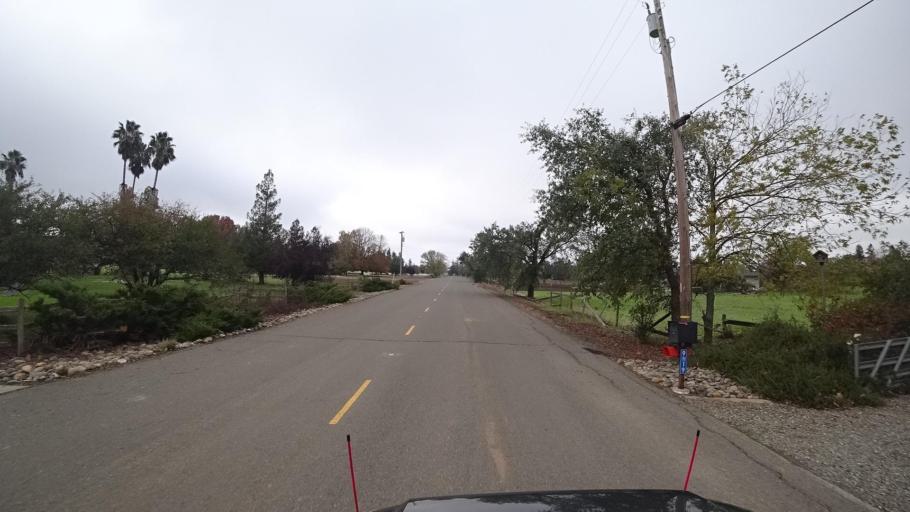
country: US
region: California
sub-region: Sacramento County
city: Elk Grove
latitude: 38.4133
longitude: -121.3247
